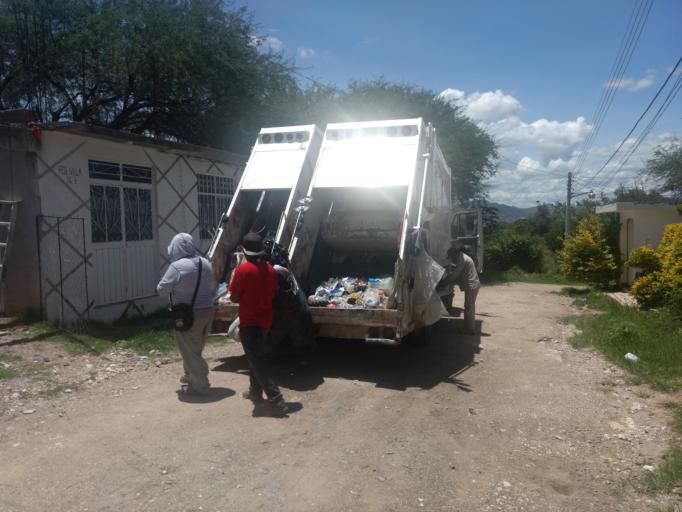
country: MX
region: Oaxaca
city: Ciudad de Huajuapam de Leon
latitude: 17.8175
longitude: -97.7934
